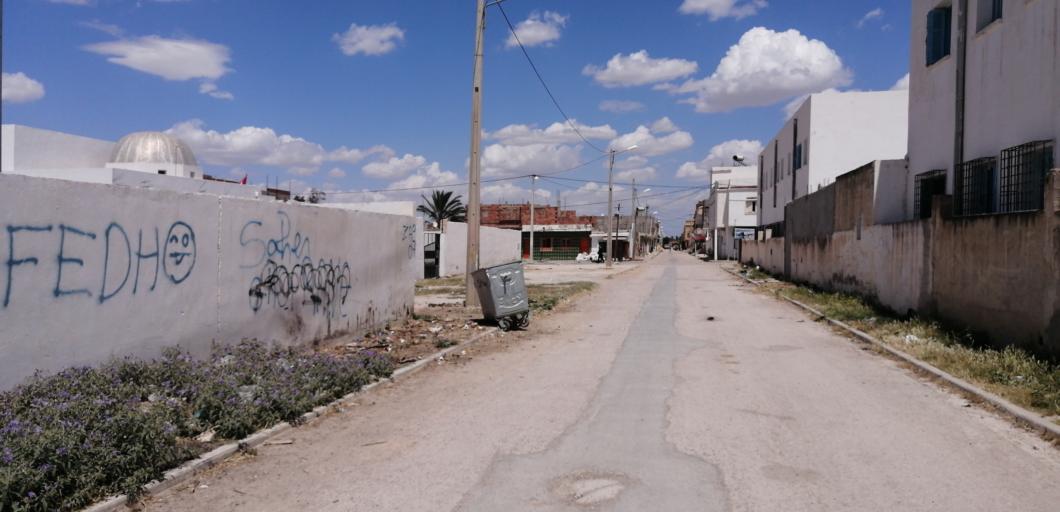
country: TN
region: Al Qayrawan
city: Kairouan
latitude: 35.6174
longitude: 9.9250
